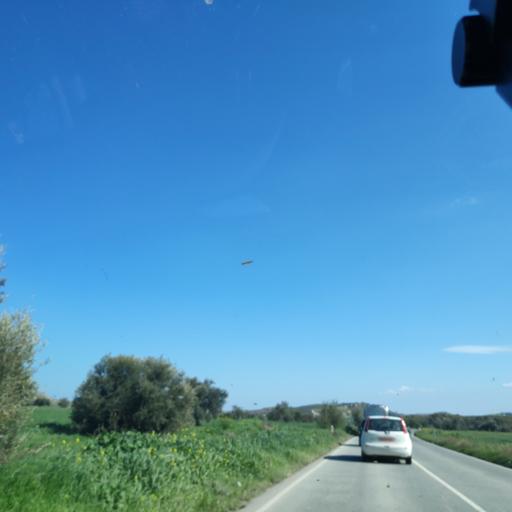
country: CY
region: Lefkosia
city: Tseri
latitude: 35.0137
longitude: 33.3408
